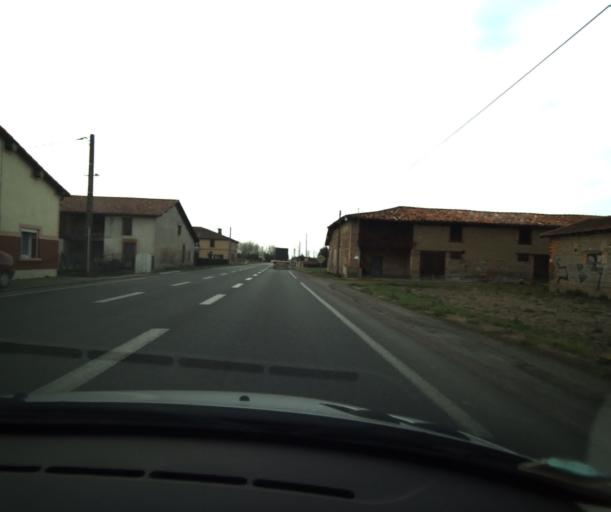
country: FR
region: Midi-Pyrenees
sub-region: Departement du Tarn-et-Garonne
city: Castelsarrasin
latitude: 44.0286
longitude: 1.1369
